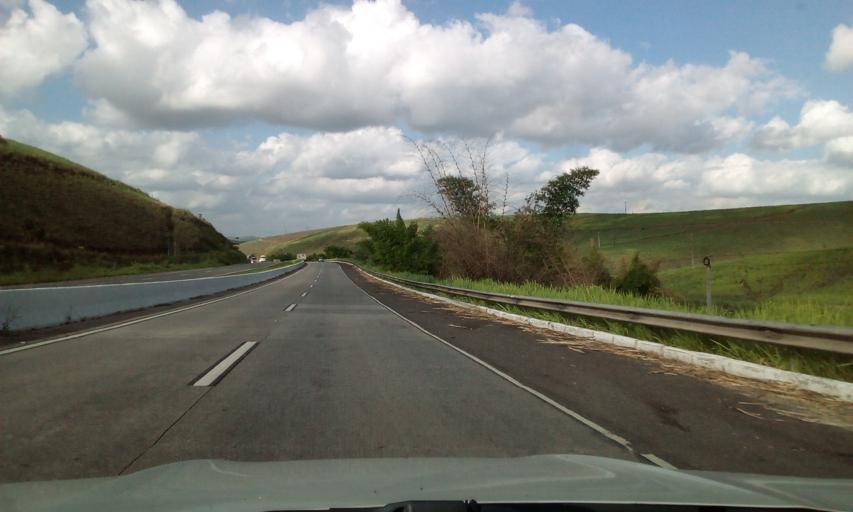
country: BR
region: Pernambuco
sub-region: Palmares
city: Palmares
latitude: -8.6531
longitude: -35.5637
